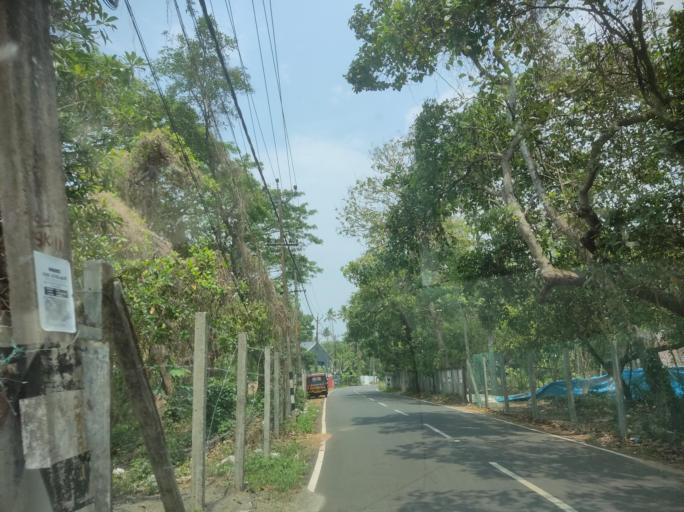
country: IN
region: Kerala
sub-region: Alappuzha
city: Vayalar
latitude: 9.6975
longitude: 76.3252
